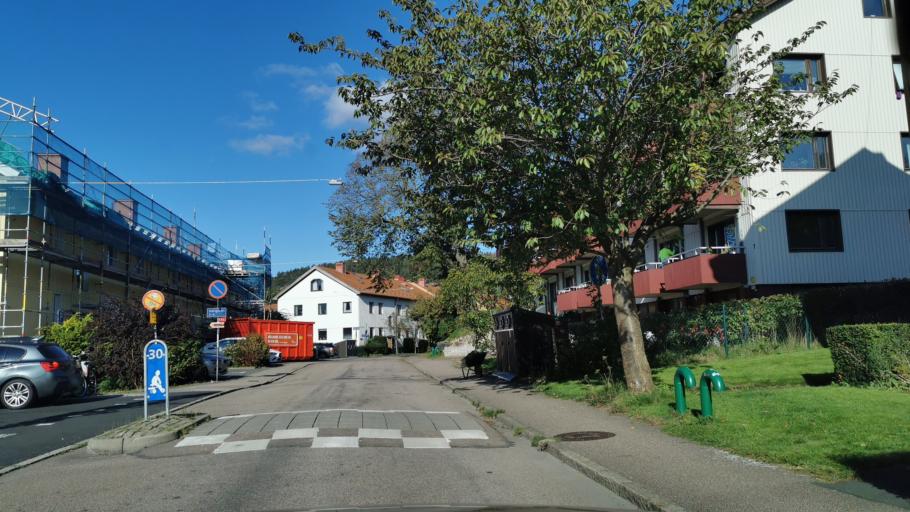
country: SE
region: Vaestra Goetaland
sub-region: Goteborg
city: Eriksbo
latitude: 57.7315
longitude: 12.0154
